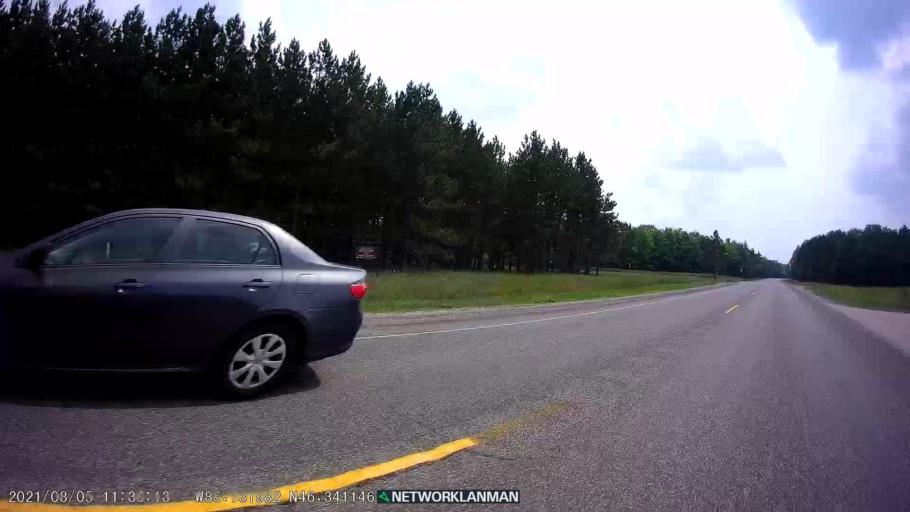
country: US
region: Michigan
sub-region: Alger County
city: Munising
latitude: 46.3425
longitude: -86.7318
